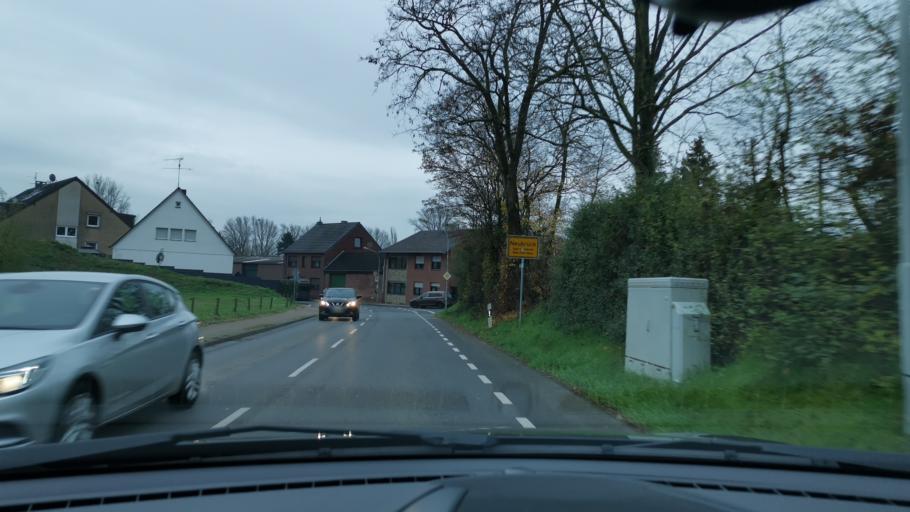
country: DE
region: North Rhine-Westphalia
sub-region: Regierungsbezirk Dusseldorf
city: Neubrueck
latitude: 51.1342
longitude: 6.6379
